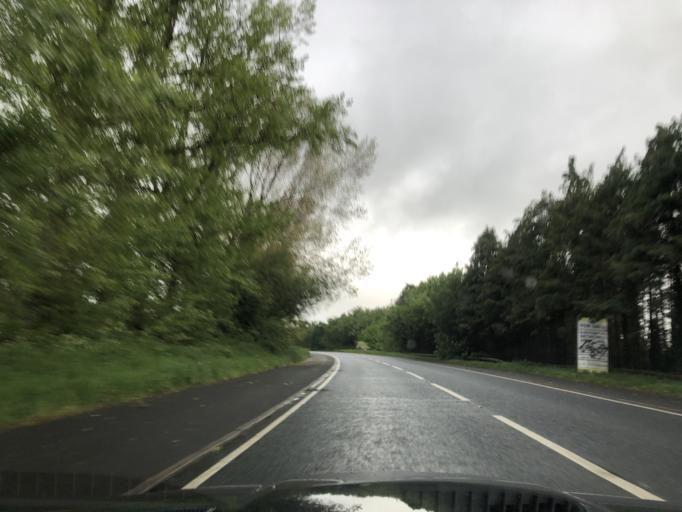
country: GB
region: Northern Ireland
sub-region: Antrim Borough
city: Antrim
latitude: 54.6870
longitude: -6.2236
